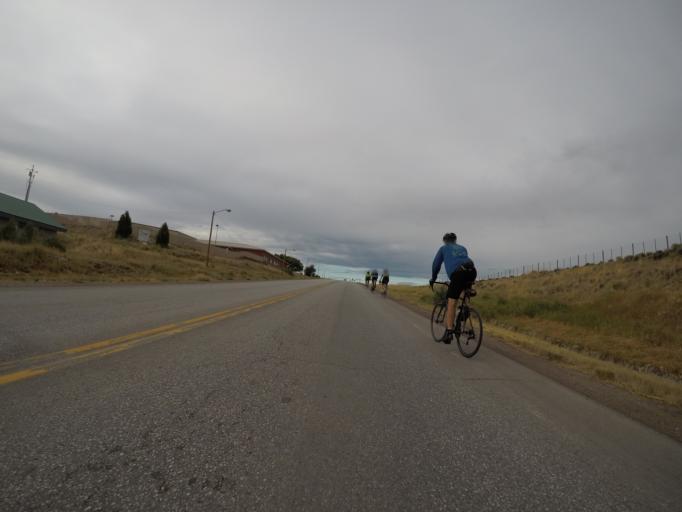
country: US
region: Wyoming
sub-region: Carbon County
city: Saratoga
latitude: 41.4491
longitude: -106.8077
